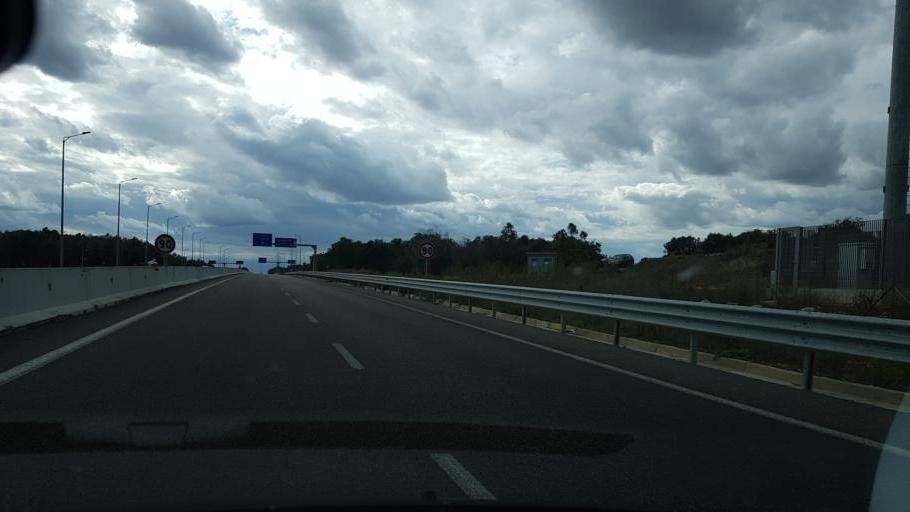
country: IT
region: Apulia
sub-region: Provincia di Lecce
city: Palmariggi
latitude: 40.1346
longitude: 18.4003
